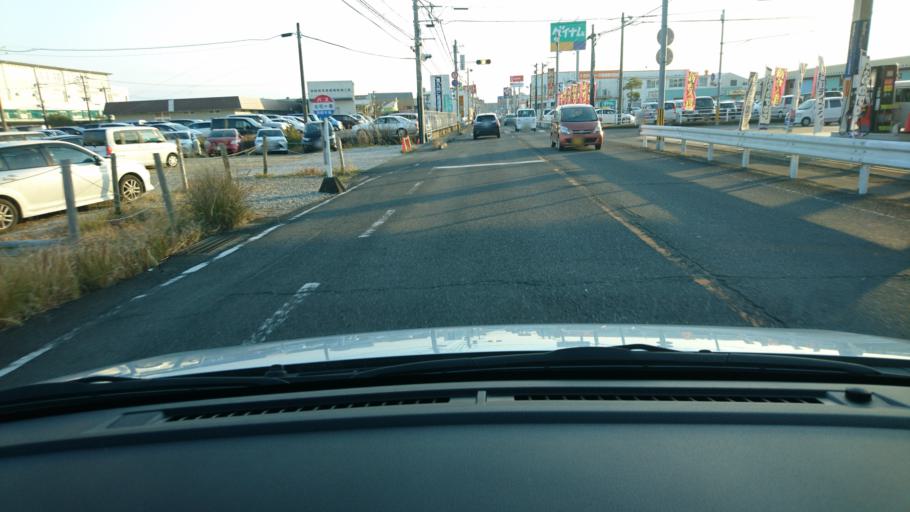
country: JP
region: Miyazaki
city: Miyazaki-shi
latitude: 31.9560
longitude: 131.4356
